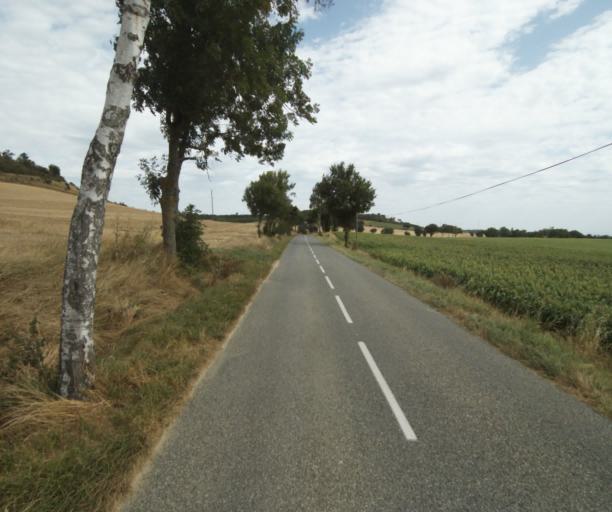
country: FR
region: Midi-Pyrenees
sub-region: Departement de la Haute-Garonne
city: Saint-Felix-Lauragais
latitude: 43.4371
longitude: 1.8978
